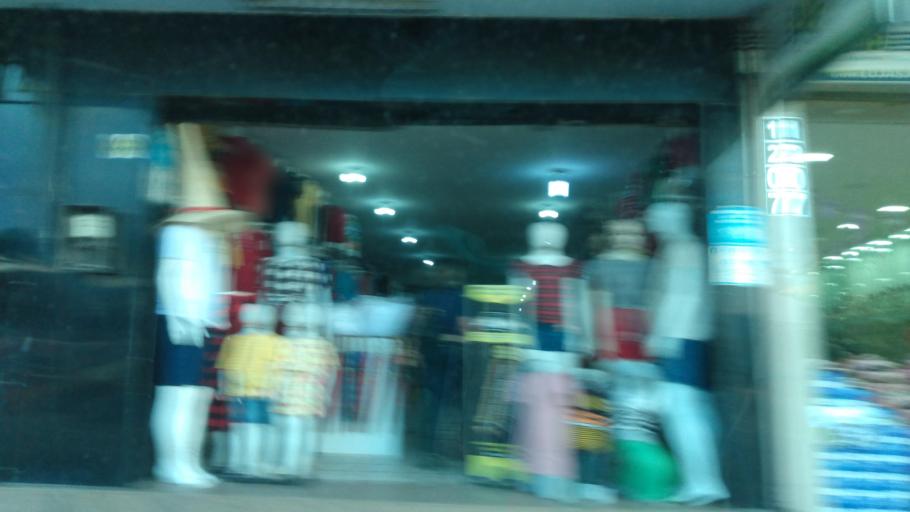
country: BR
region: Pernambuco
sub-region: Palmares
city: Palmares
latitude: -8.6847
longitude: -35.5893
